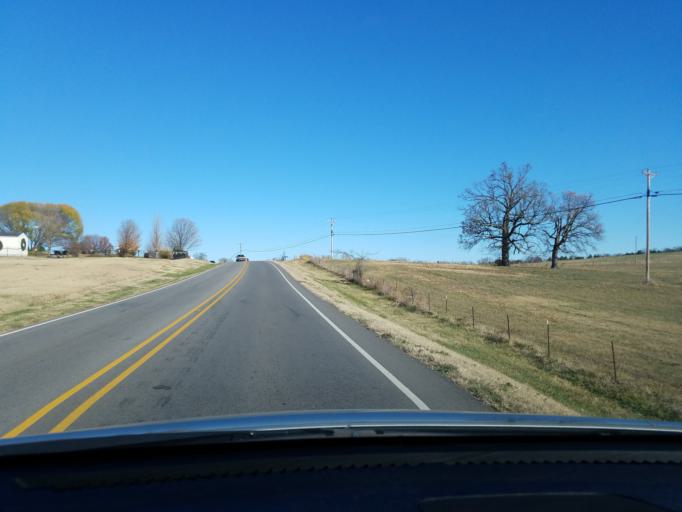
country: US
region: Arkansas
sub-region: Carroll County
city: Berryville
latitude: 36.3845
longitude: -93.5669
